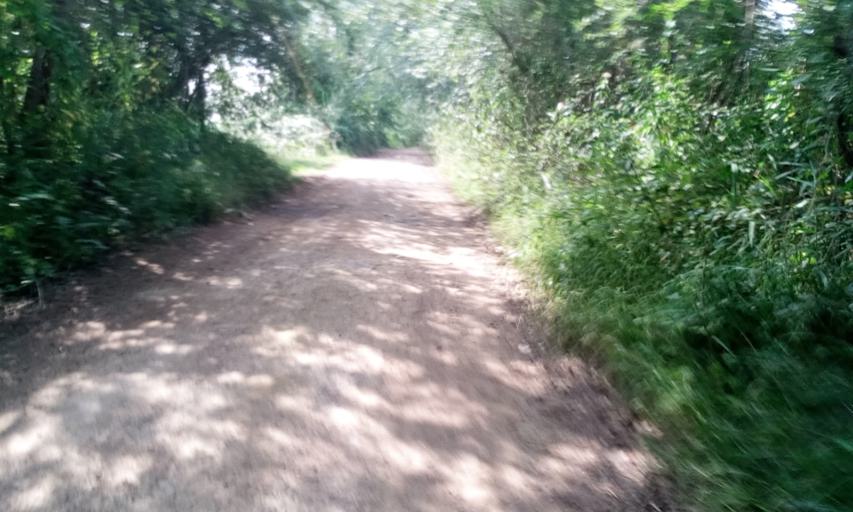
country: FR
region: Lower Normandy
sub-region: Departement du Calvados
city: Bellengreville
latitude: 49.1434
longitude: -0.1950
